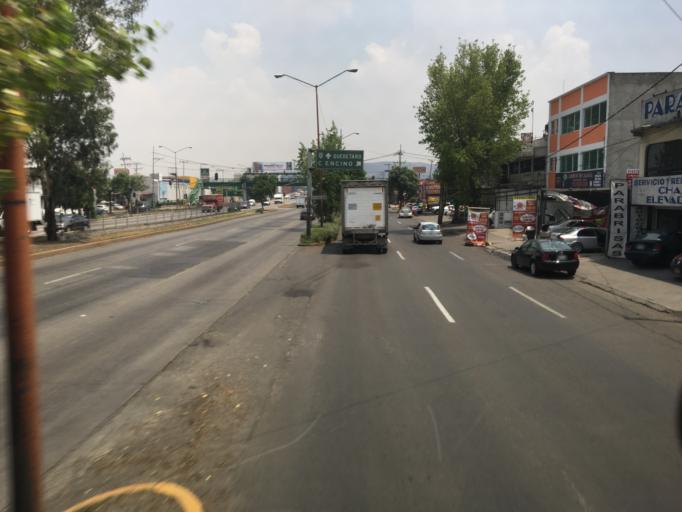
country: MX
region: Mexico
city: Tlalnepantla
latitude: 19.5427
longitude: -99.1823
